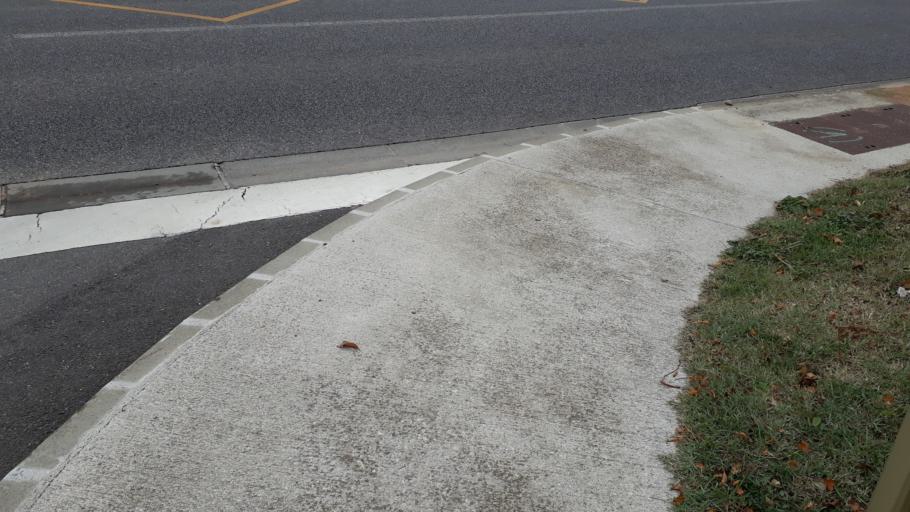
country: FR
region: Midi-Pyrenees
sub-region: Departement de la Haute-Garonne
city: Cornebarrieu
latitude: 43.6500
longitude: 1.3235
